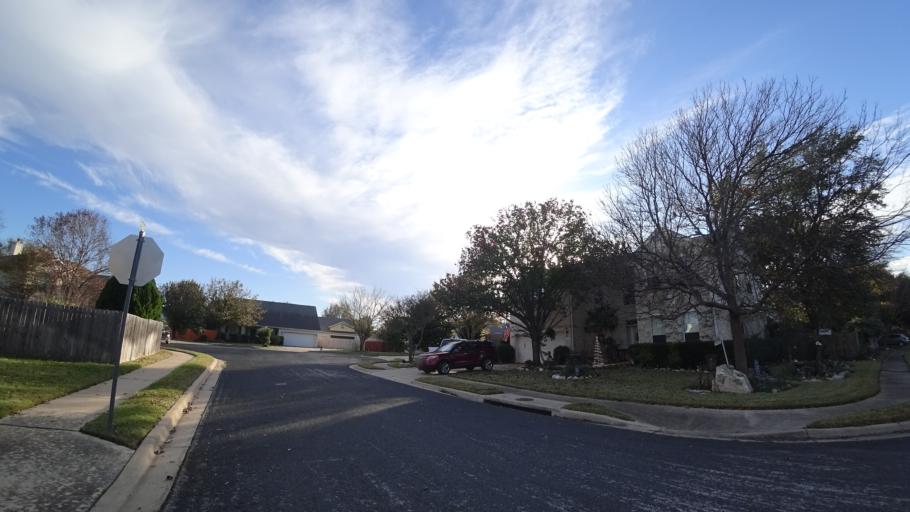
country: US
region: Texas
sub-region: Williamson County
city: Brushy Creek
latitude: 30.5029
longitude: -97.7325
